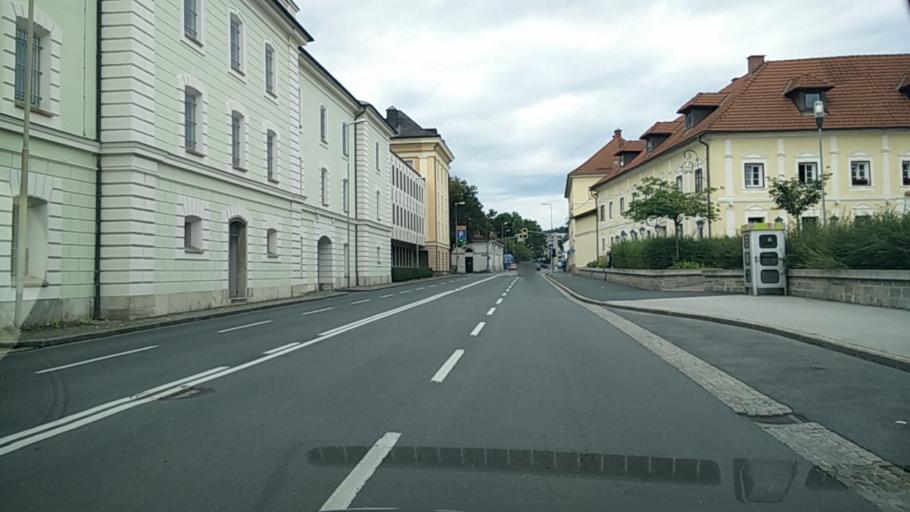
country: AT
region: Carinthia
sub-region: Klagenfurt am Woerthersee
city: Klagenfurt am Woerthersee
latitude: 46.6280
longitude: 14.3080
